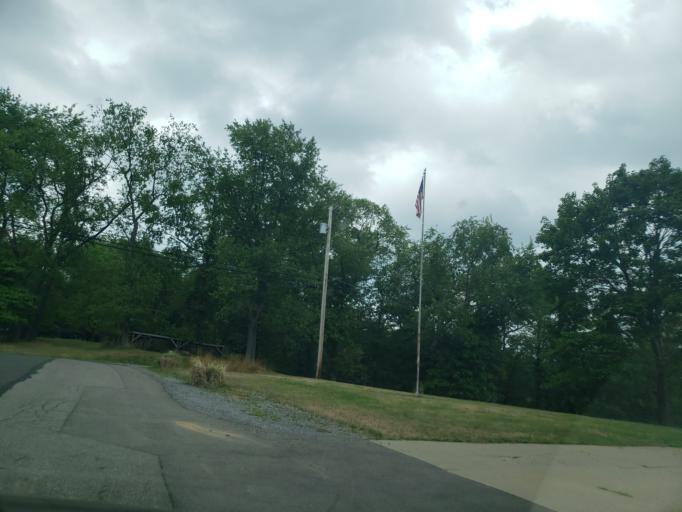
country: US
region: Pennsylvania
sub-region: Allegheny County
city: Coraopolis
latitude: 40.5340
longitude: -80.1597
